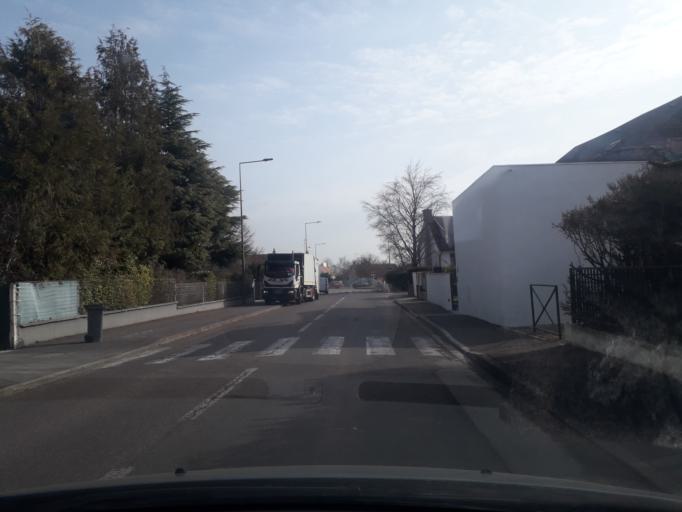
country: FR
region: Bourgogne
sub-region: Departement de la Cote-d'Or
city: Fontaine-les-Dijon
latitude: 47.3394
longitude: 5.0188
